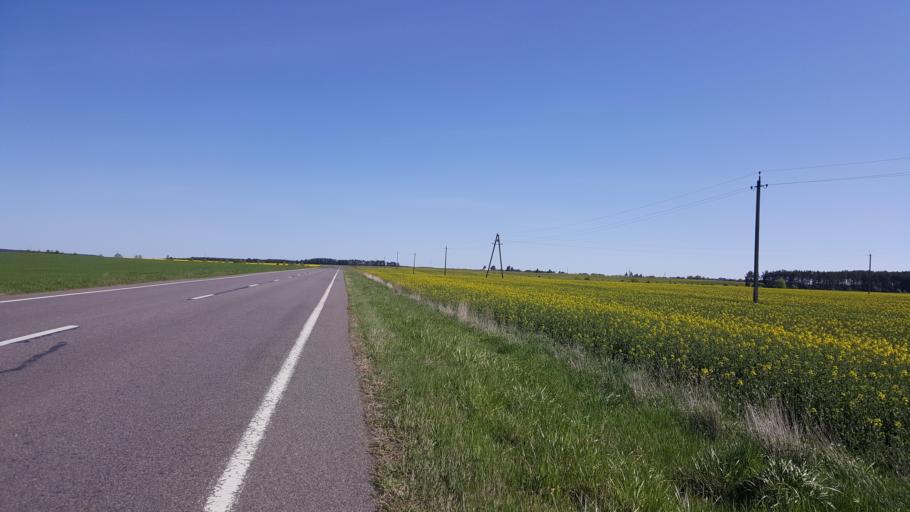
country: BY
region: Brest
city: Kamyanyets
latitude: 52.4175
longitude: 23.8464
